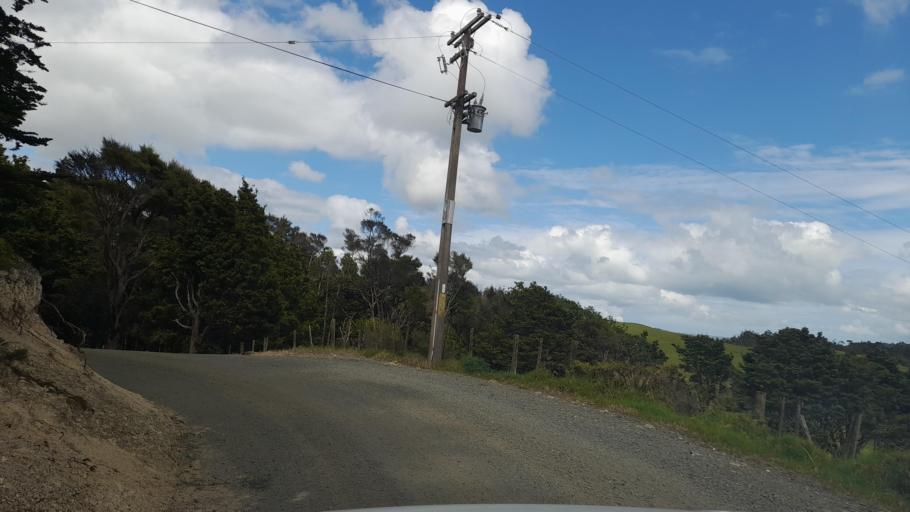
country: NZ
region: Auckland
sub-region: Auckland
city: Wellsford
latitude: -36.2147
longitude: 174.3195
